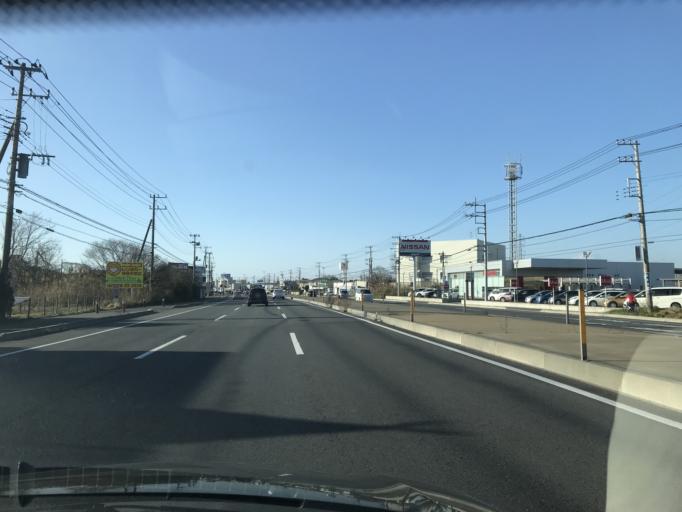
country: JP
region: Chiba
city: Omigawa
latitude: 35.8791
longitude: 140.6852
